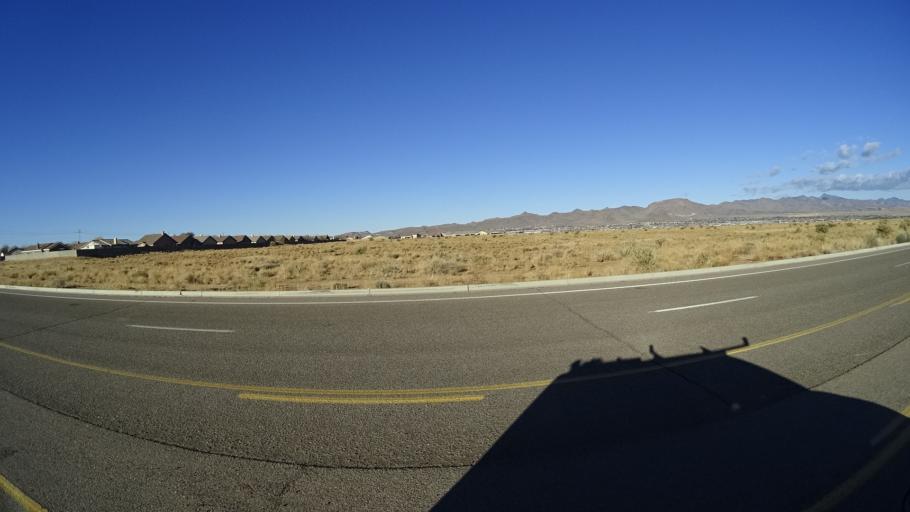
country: US
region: Arizona
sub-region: Mohave County
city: New Kingman-Butler
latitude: 35.2265
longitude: -113.9760
